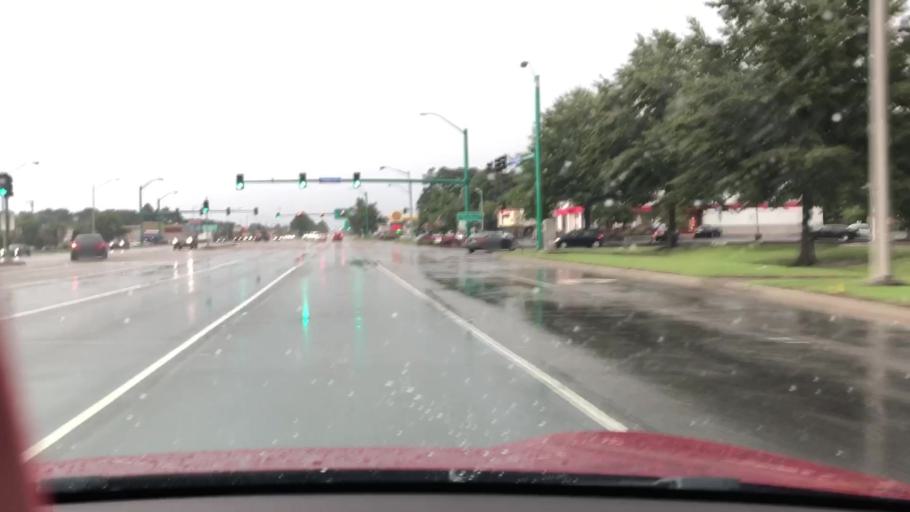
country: US
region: Virginia
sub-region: City of Chesapeake
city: Chesapeake
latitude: 36.8472
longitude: -76.2100
